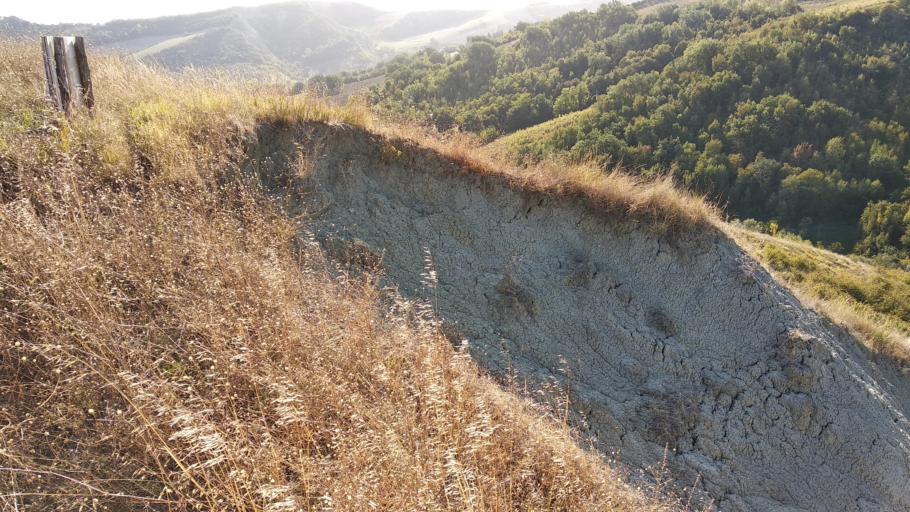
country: IT
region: Emilia-Romagna
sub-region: Provincia di Bologna
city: Borgo Tossignano
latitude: 44.3283
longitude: 11.5622
